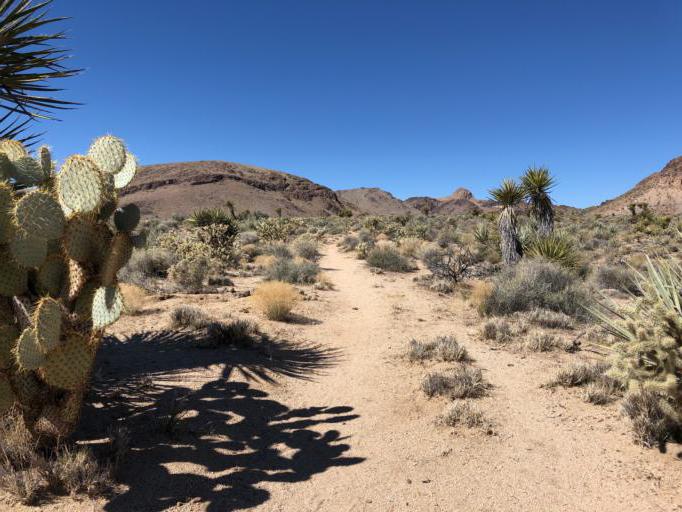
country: US
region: Nevada
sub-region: Clark County
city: Sandy Valley
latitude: 35.0397
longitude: -115.4063
